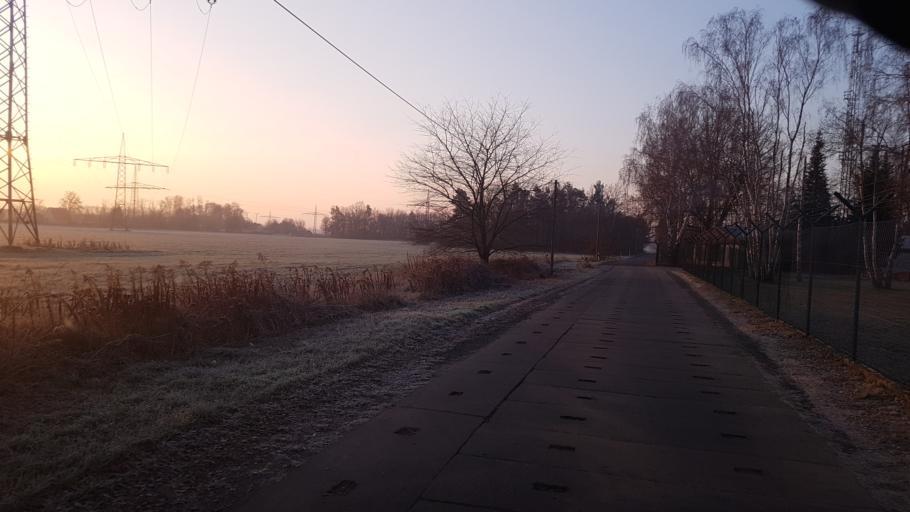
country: DE
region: Brandenburg
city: Lauchhammer
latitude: 51.4803
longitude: 13.7222
